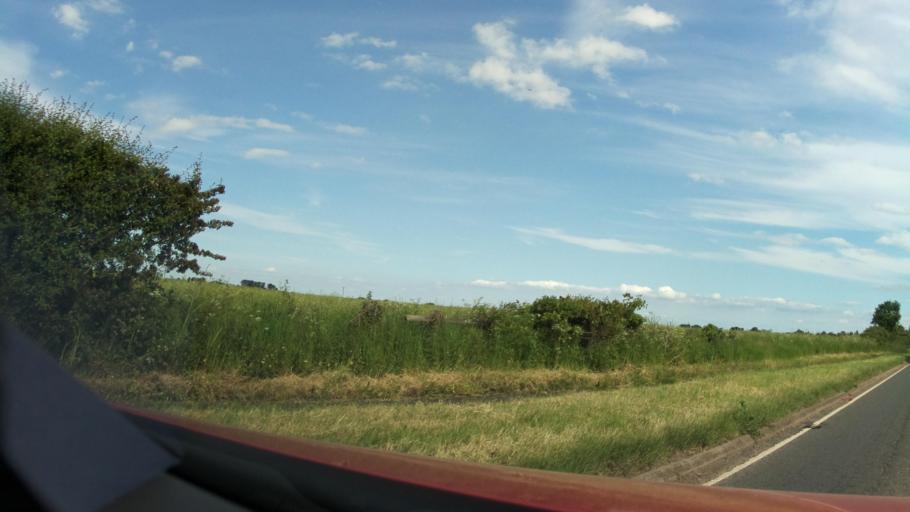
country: GB
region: England
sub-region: Worcestershire
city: Kempsey
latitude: 52.1529
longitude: -2.1501
